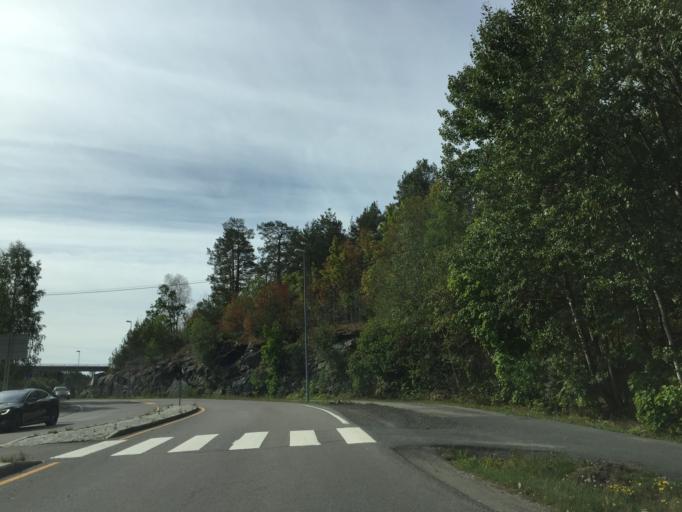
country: NO
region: Ostfold
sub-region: Moss
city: Moss
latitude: 59.5213
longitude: 10.6960
